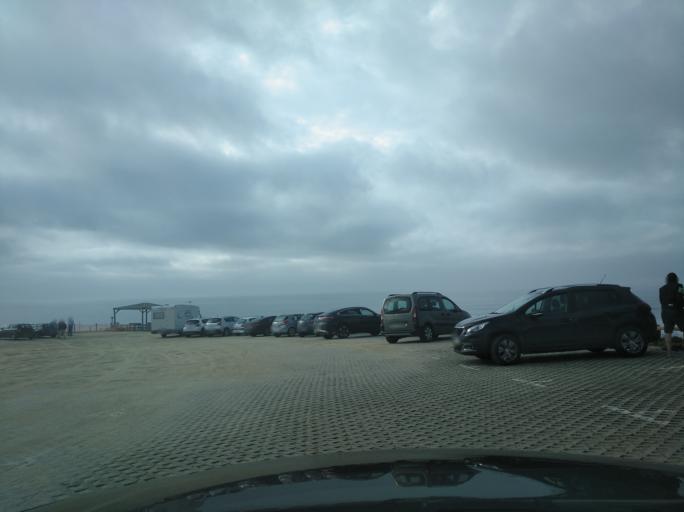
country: PT
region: Beja
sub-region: Odemira
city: Vila Nova de Milfontes
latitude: 37.6534
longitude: -8.8010
